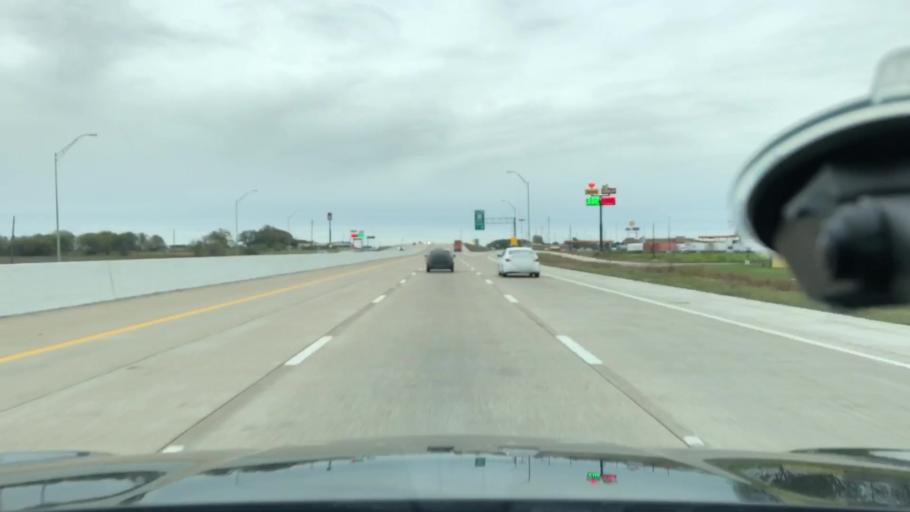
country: US
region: Texas
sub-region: Ellis County
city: Italy
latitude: 32.1905
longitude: -96.9019
